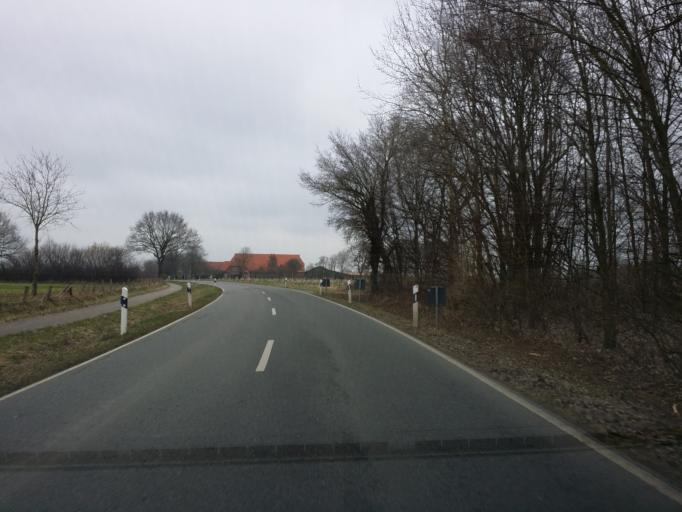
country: DE
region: Schleswig-Holstein
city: Hassmoor
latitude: 54.3138
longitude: 9.7946
